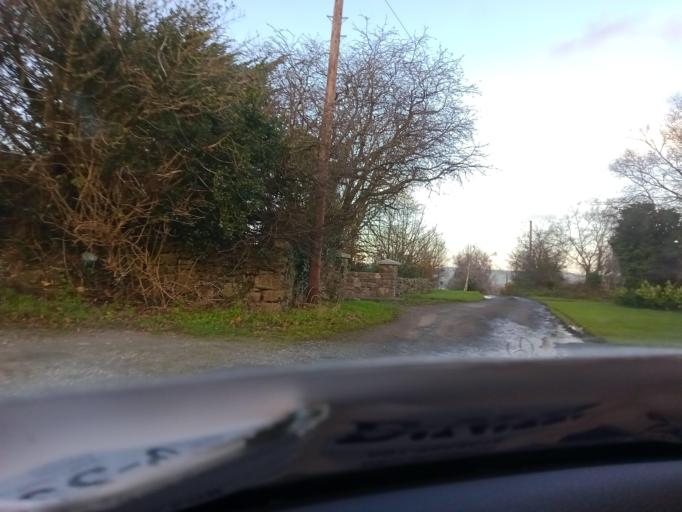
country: IE
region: Munster
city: Carrick-on-Suir
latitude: 52.3342
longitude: -7.4088
